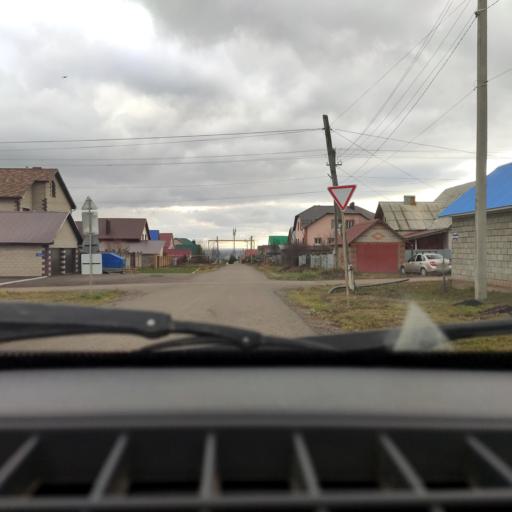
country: RU
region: Bashkortostan
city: Mikhaylovka
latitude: 54.8186
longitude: 55.8901
